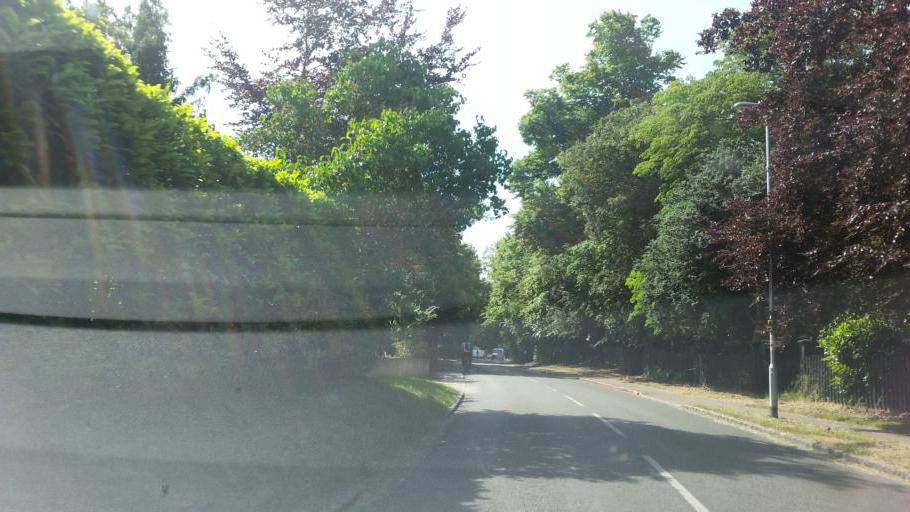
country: GB
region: England
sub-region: Cambridgeshire
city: Sawston
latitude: 52.1476
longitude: 0.1480
